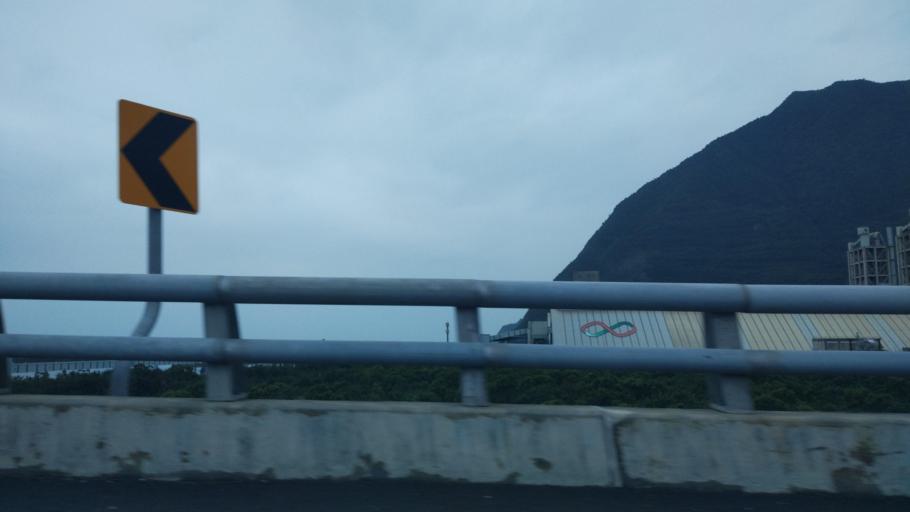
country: TW
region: Taiwan
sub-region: Hualien
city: Hualian
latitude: 24.3106
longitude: 121.7577
